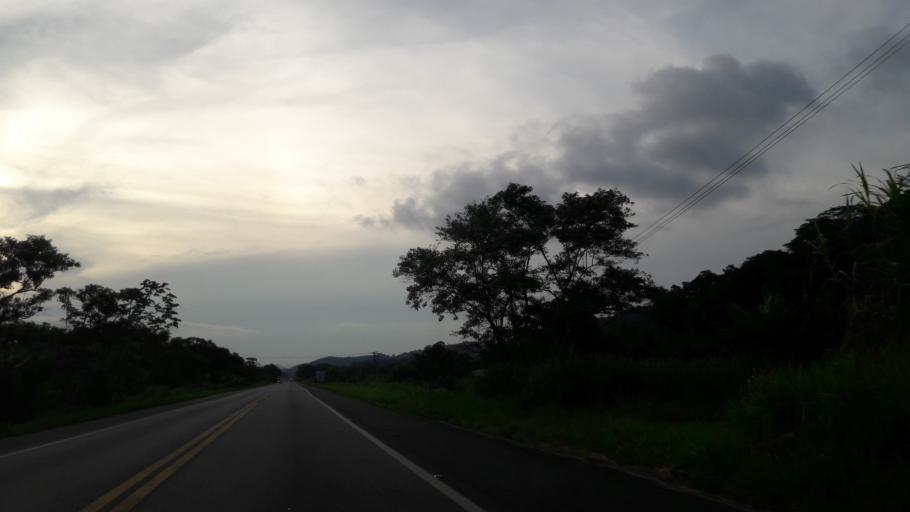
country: BR
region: Sao Paulo
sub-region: Peruibe
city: Peruibe
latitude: -24.2982
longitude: -47.0591
